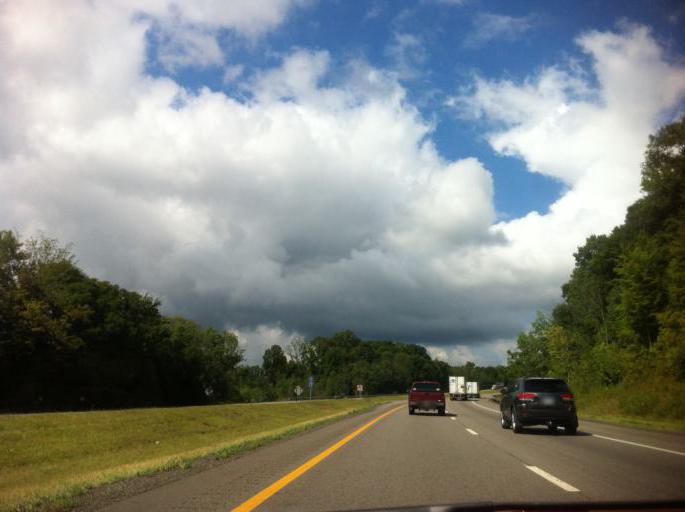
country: US
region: Ohio
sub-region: Trumbull County
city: Churchill
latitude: 41.1589
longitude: -80.6232
